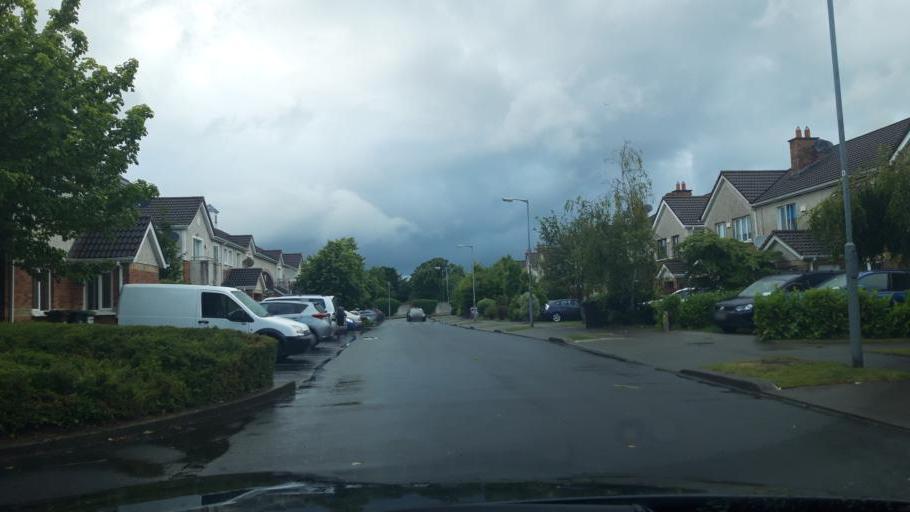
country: IE
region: Leinster
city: Hartstown
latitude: 53.3984
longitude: -6.4397
